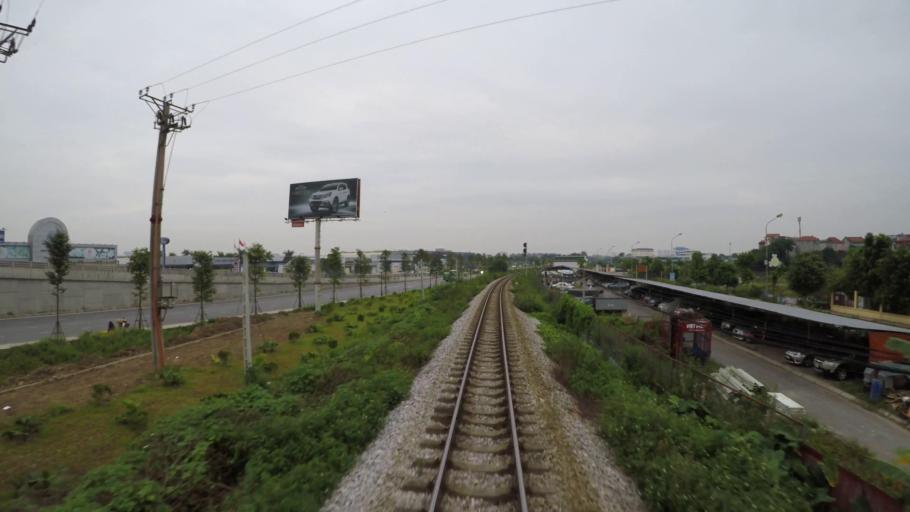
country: VN
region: Ha Noi
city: Trau Quy
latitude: 21.0172
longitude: 105.9436
